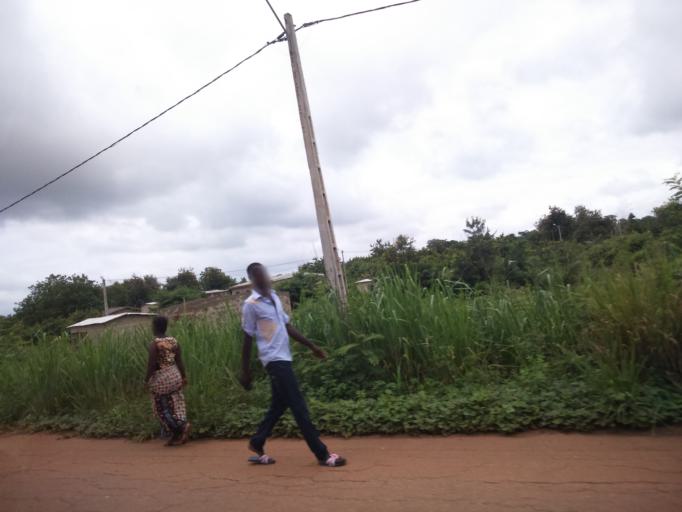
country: CI
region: Moyen-Comoe
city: Abengourou
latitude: 6.6343
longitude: -3.7103
